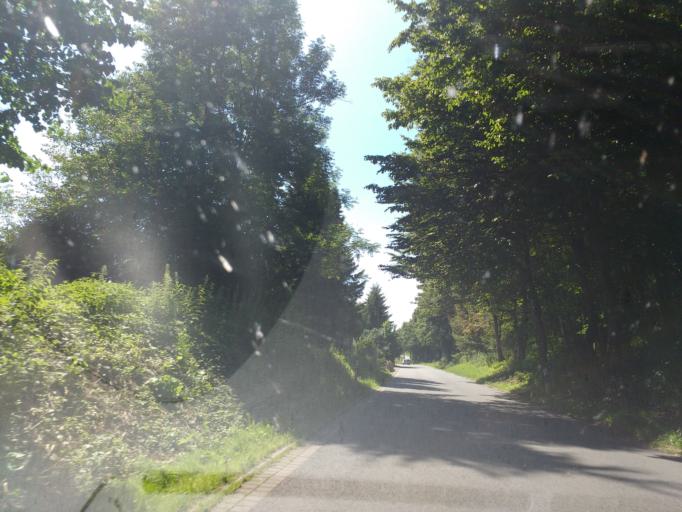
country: DE
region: North Rhine-Westphalia
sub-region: Regierungsbezirk Detmold
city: Horn
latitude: 51.8245
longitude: 8.9307
